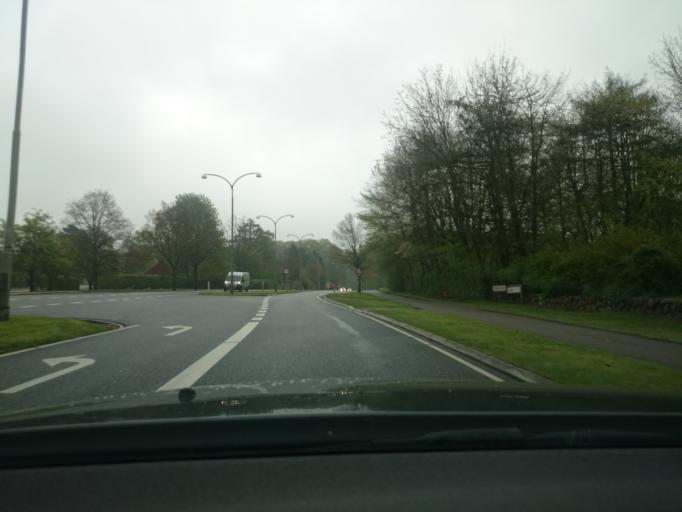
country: DK
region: Capital Region
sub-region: Lyngby-Tarbaek Kommune
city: Kongens Lyngby
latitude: 55.7746
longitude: 12.5355
